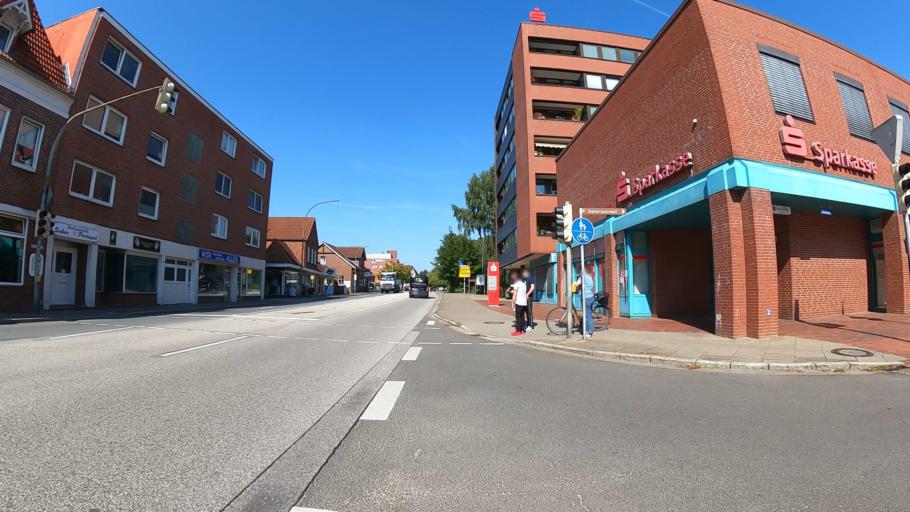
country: DE
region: Schleswig-Holstein
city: Bad Bramstedt
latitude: 53.9187
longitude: 9.8824
